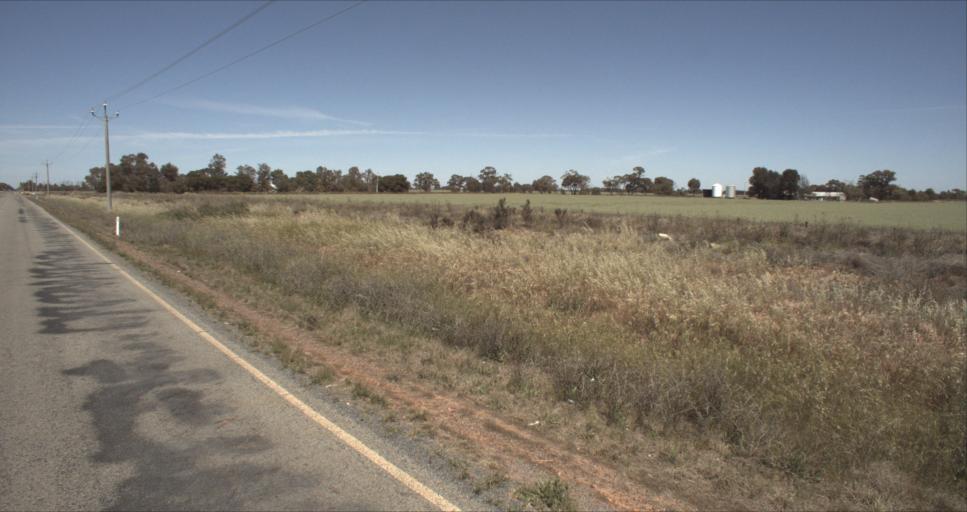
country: AU
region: New South Wales
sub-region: Leeton
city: Leeton
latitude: -34.5112
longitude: 146.2851
